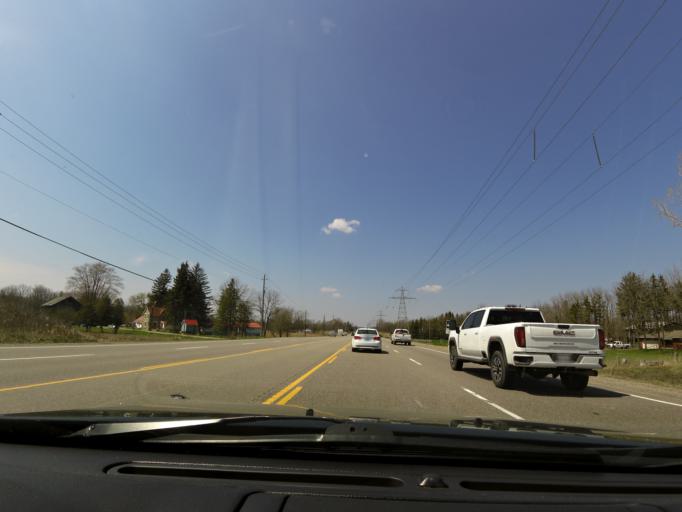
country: CA
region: Ontario
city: Ancaster
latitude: 43.3583
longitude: -79.9806
